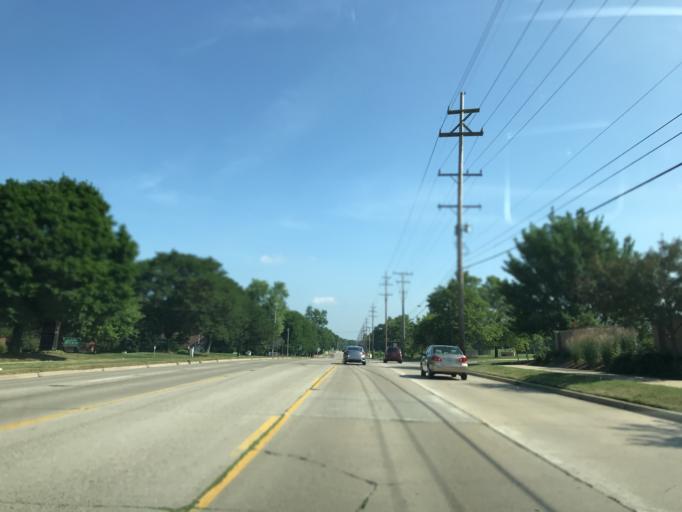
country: US
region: Michigan
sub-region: Ingham County
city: Okemos
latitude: 42.6997
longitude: -84.4324
